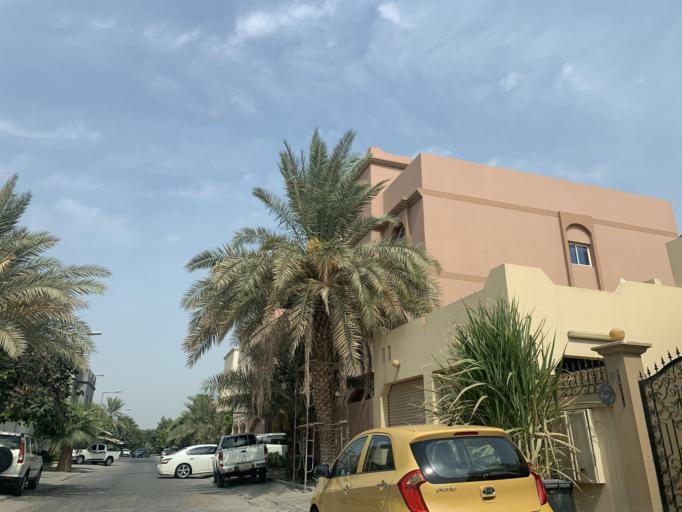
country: BH
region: Manama
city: Jidd Hafs
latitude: 26.2113
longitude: 50.4912
